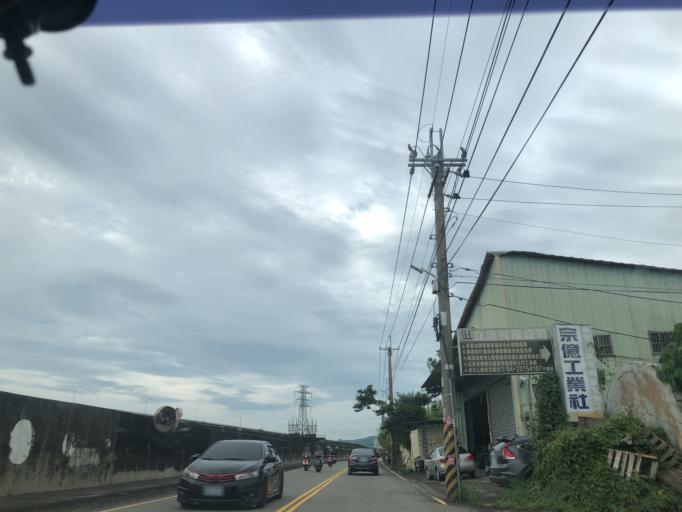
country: TW
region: Taiwan
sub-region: Taichung City
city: Taichung
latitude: 24.1229
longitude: 120.7040
